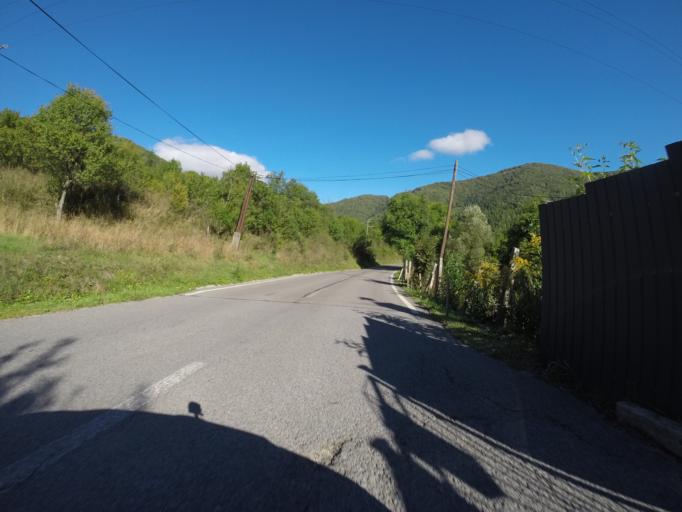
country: SK
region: Trenciansky
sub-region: Okres Povazska Bystrica
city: Povazska Bystrica
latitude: 48.9575
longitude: 18.4112
